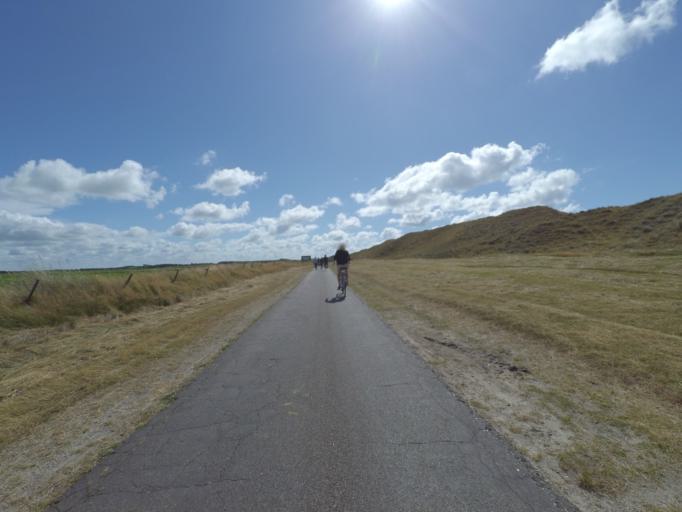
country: NL
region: North Holland
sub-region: Gemeente Texel
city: Den Burg
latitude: 53.1182
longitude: 4.8018
